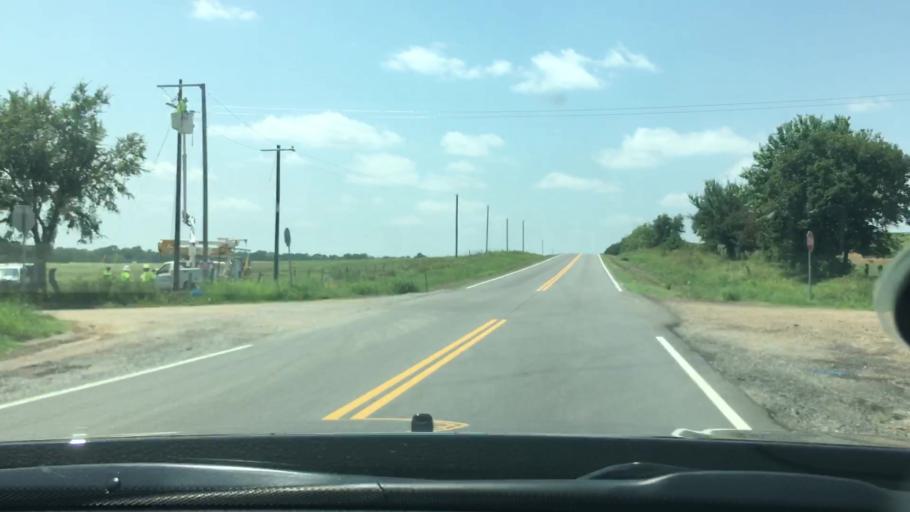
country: US
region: Oklahoma
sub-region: Atoka County
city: Atoka
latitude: 34.3750
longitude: -96.2149
